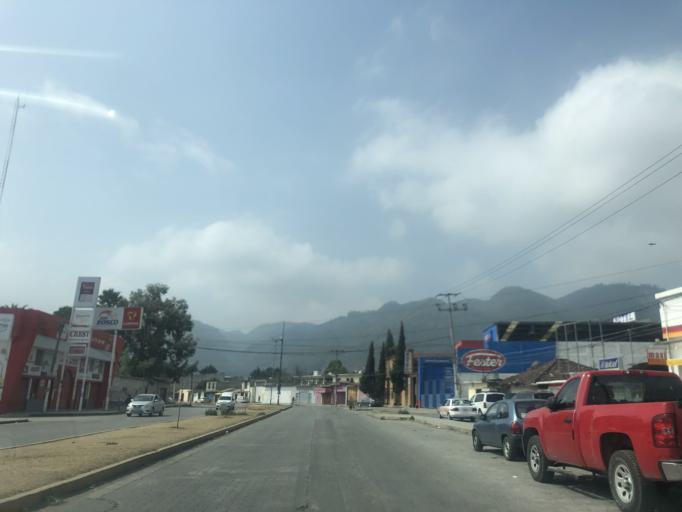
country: MX
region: Chiapas
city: San Cristobal de las Casas
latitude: 16.7183
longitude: -92.6370
